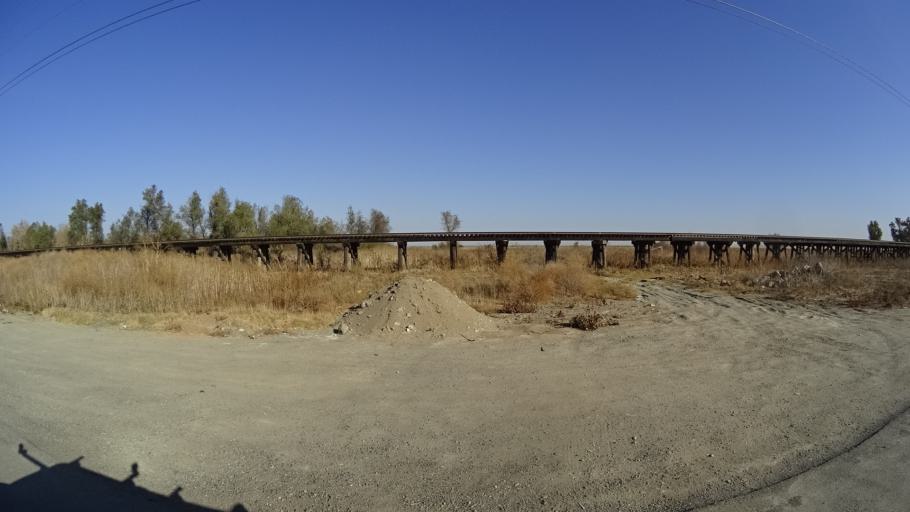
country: US
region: California
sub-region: Yolo County
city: Woodland
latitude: 38.6766
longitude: -121.6703
